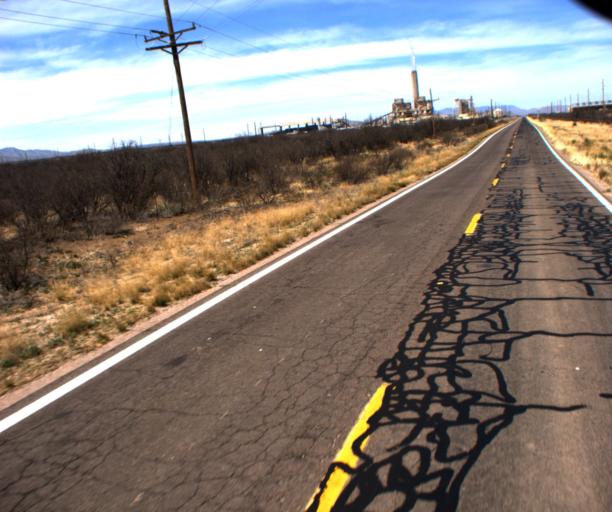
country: US
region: Arizona
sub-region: Cochise County
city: Willcox
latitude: 32.0510
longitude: -109.8865
